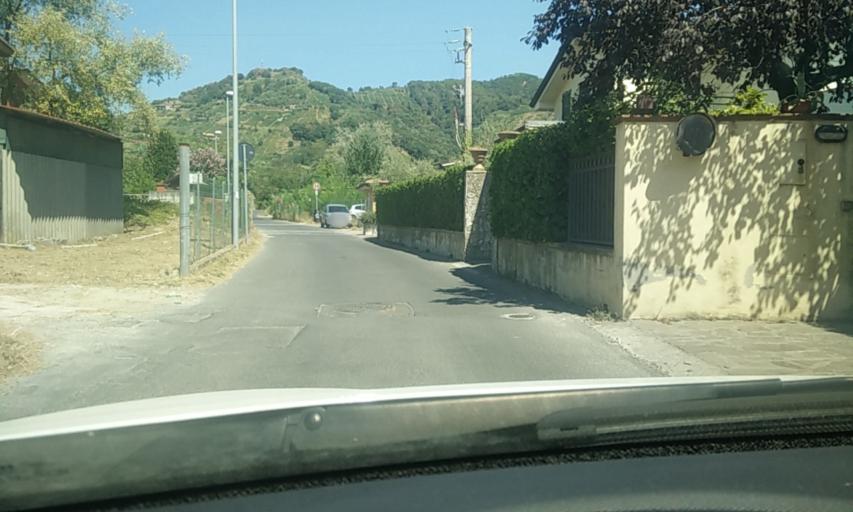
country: IT
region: Tuscany
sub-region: Provincia di Massa-Carrara
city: Massa
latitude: 44.0407
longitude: 10.1033
